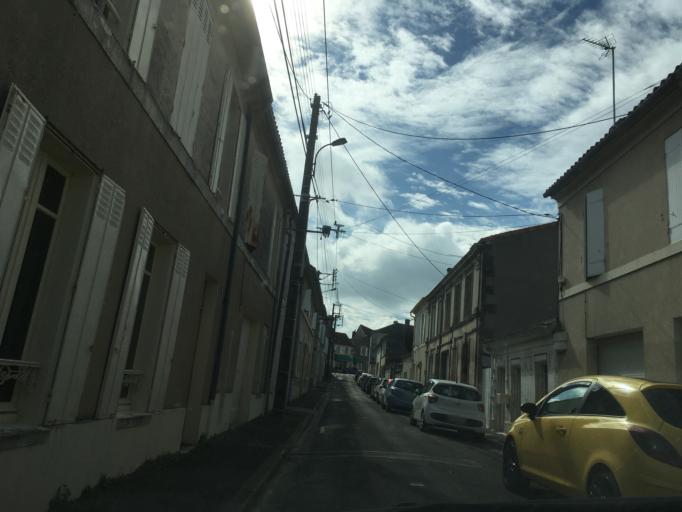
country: FR
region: Poitou-Charentes
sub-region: Departement de la Charente
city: Cognac
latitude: 45.6868
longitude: -0.3303
